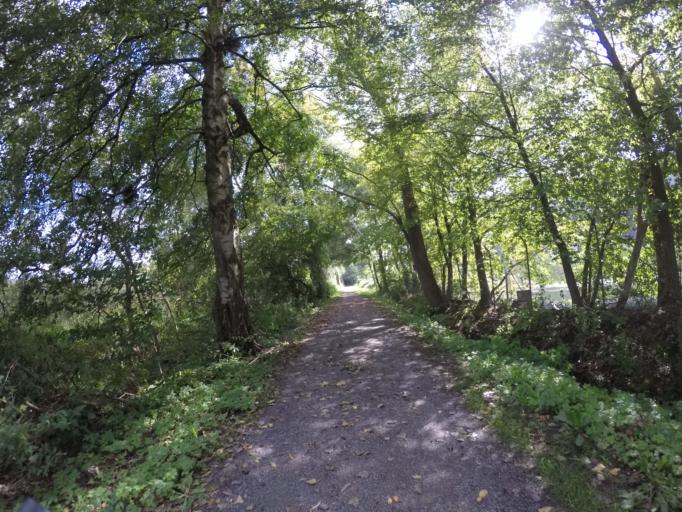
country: DE
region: North Rhine-Westphalia
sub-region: Regierungsbezirk Detmold
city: Hiddenhausen
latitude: 52.1355
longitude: 8.6374
